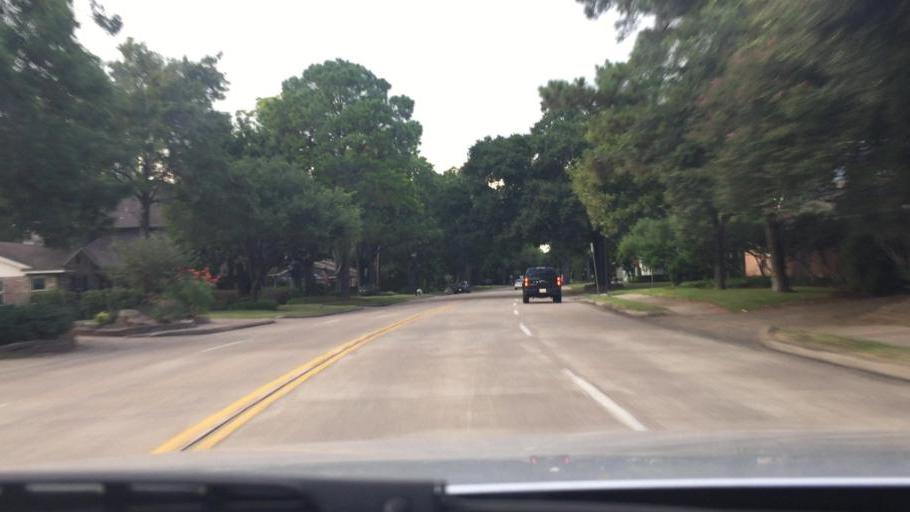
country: US
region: Texas
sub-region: Harris County
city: Hunters Creek Village
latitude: 29.7400
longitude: -95.4769
